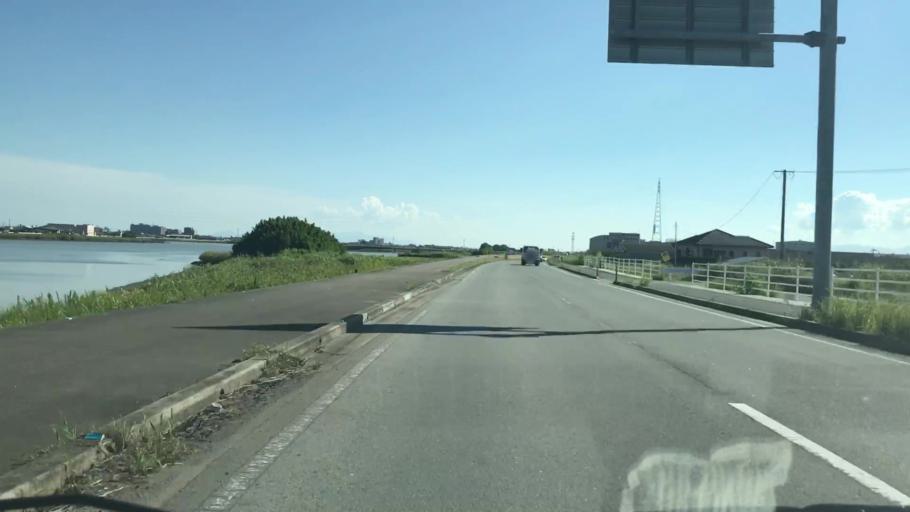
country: JP
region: Saga Prefecture
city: Okawa
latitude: 33.2352
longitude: 130.3797
